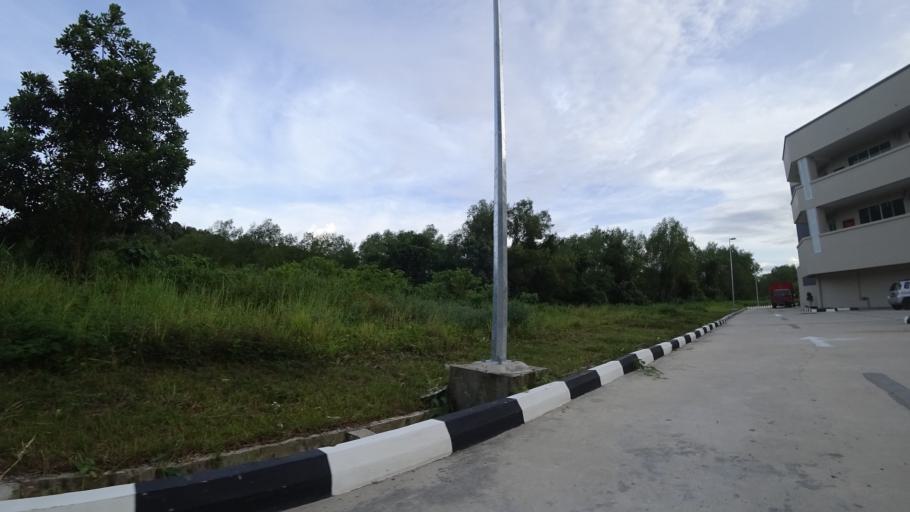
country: BN
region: Brunei and Muara
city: Bandar Seri Begawan
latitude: 4.8604
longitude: 114.8646
